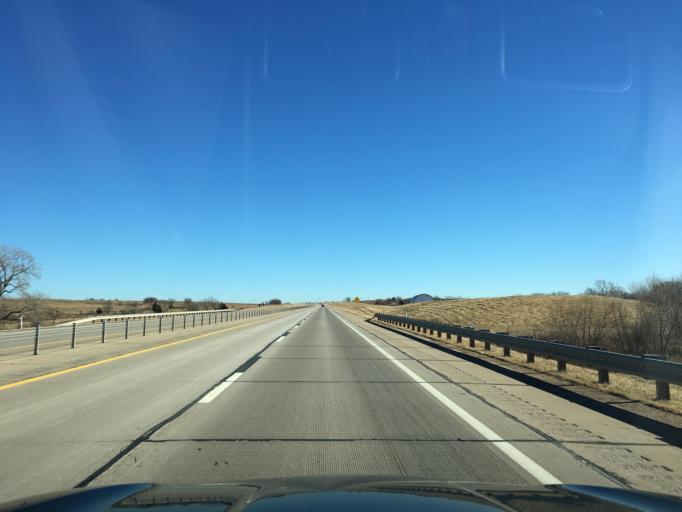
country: US
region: Oklahoma
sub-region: Noble County
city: Perry
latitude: 36.3927
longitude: -97.1929
